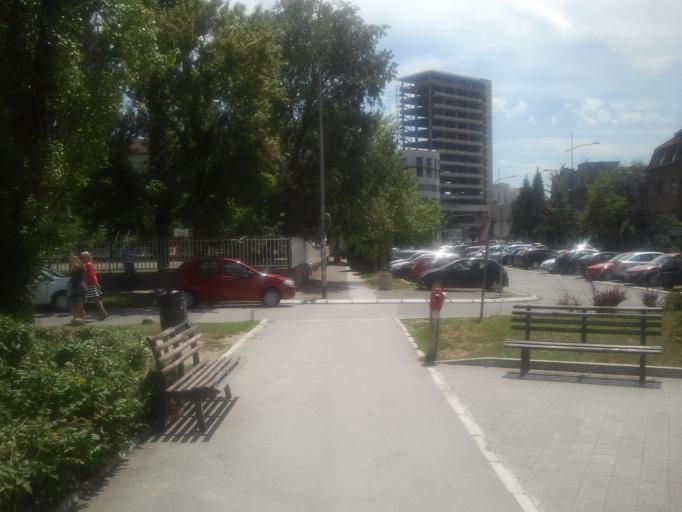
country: RS
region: Autonomna Pokrajina Vojvodina
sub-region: Juznobacki Okrug
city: Novi Sad
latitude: 45.2526
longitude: 19.8478
